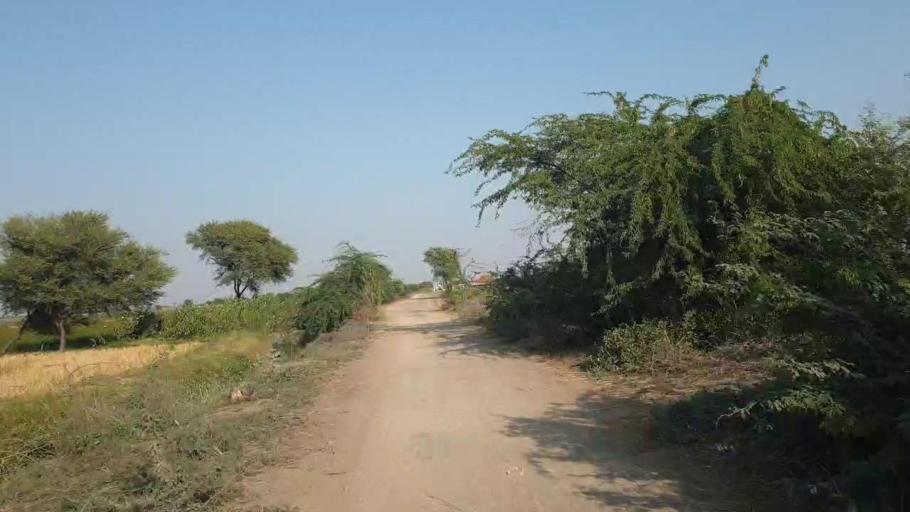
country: PK
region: Sindh
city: Kario
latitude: 24.8966
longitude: 68.6215
